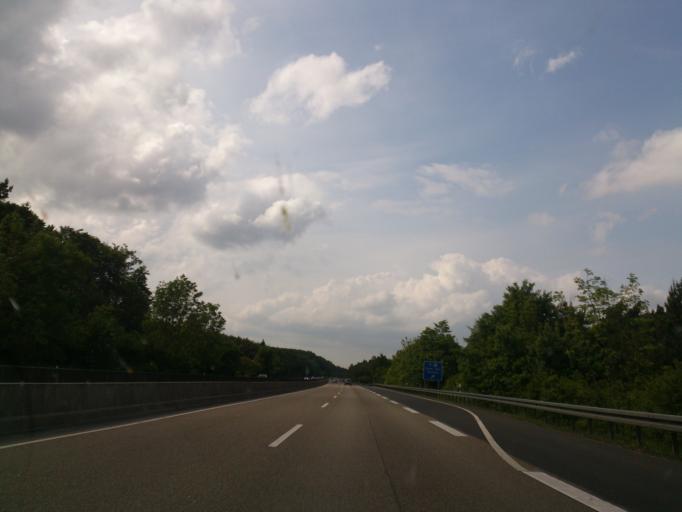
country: DE
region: Hesse
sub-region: Regierungsbezirk Kassel
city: Volkmarsen
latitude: 51.4405
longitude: 9.1474
